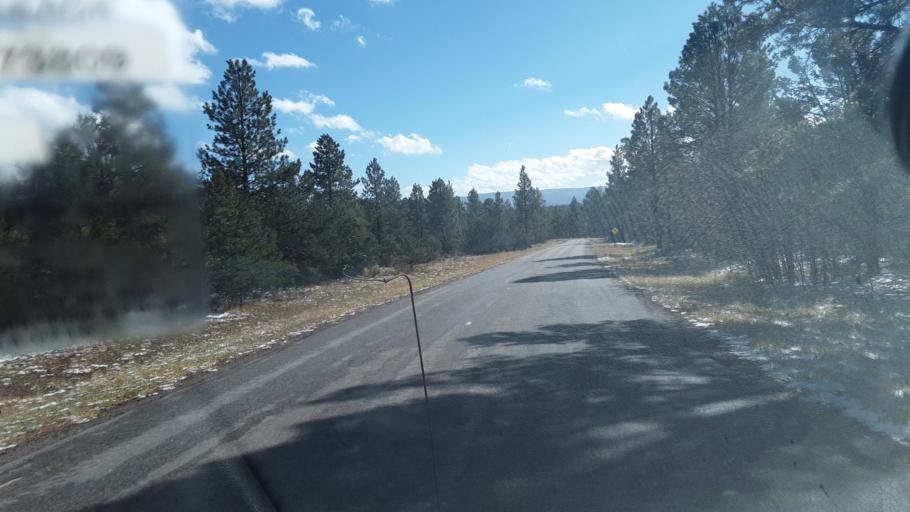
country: US
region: New Mexico
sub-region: Rio Arriba County
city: Santa Teresa
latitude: 36.1973
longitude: -106.7468
